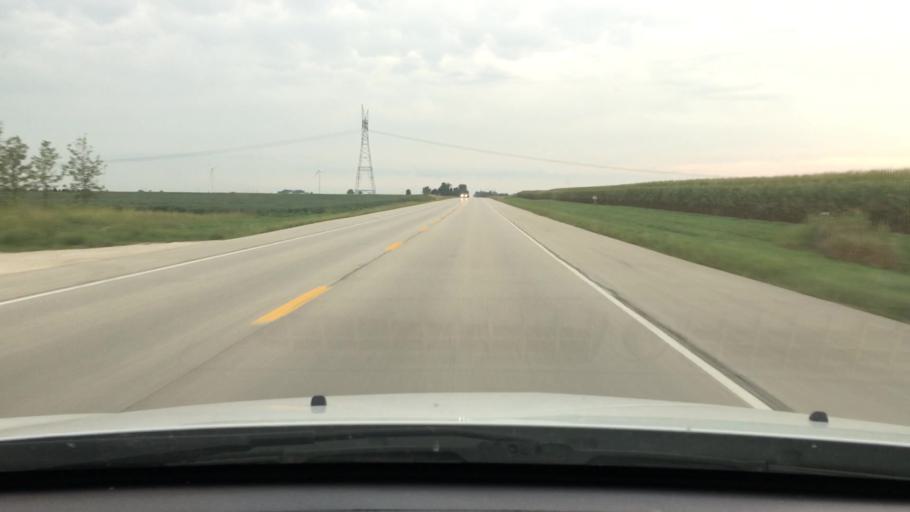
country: US
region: Illinois
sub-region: DeKalb County
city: Waterman
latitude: 41.7987
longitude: -88.7540
